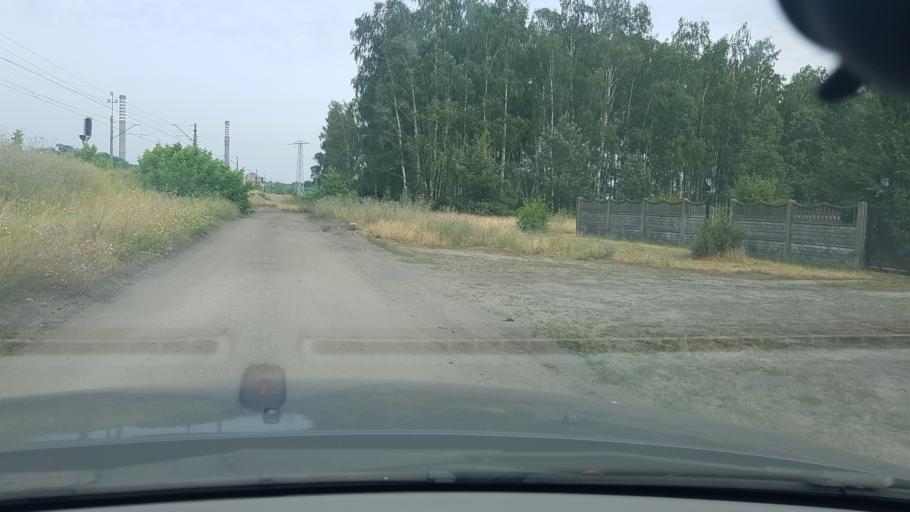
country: PL
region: Lodz Voivodeship
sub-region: Powiat tomaszowski
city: Tomaszow Mazowiecki
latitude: 51.5531
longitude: 20.0226
